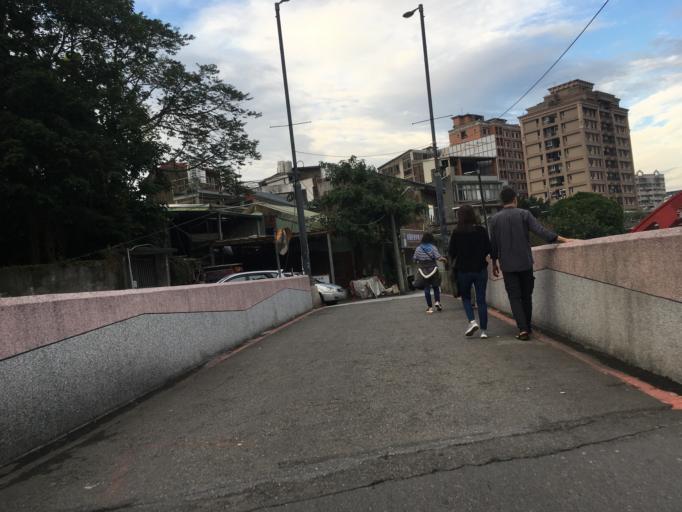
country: TW
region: Taiwan
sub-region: Taoyuan
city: Taoyuan
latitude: 24.9327
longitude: 121.3699
